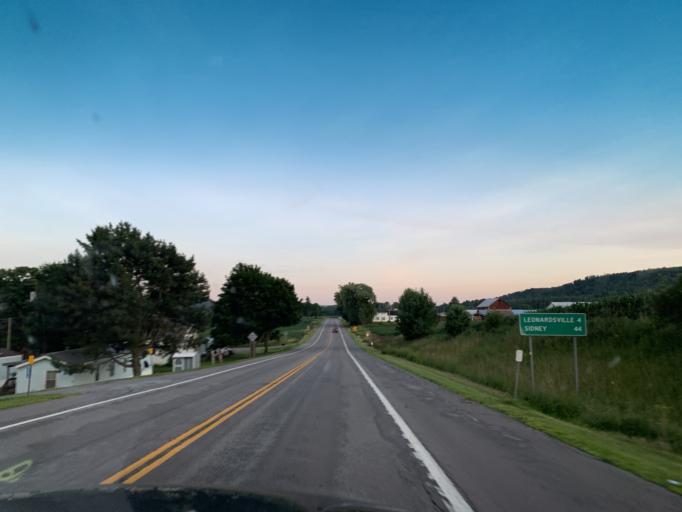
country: US
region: New York
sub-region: Oneida County
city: Waterville
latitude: 42.8707
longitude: -75.2503
